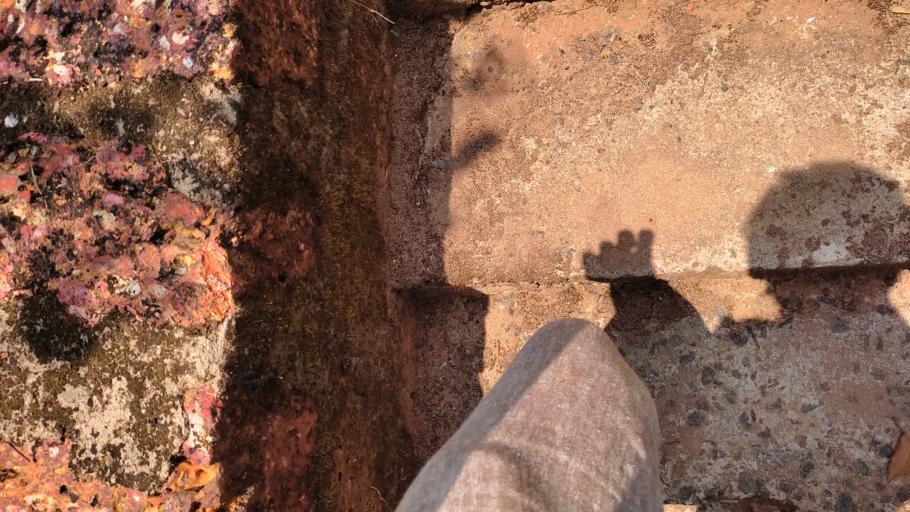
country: IN
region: Kerala
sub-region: Malappuram
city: Ponnani
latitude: 10.8283
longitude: 76.0234
